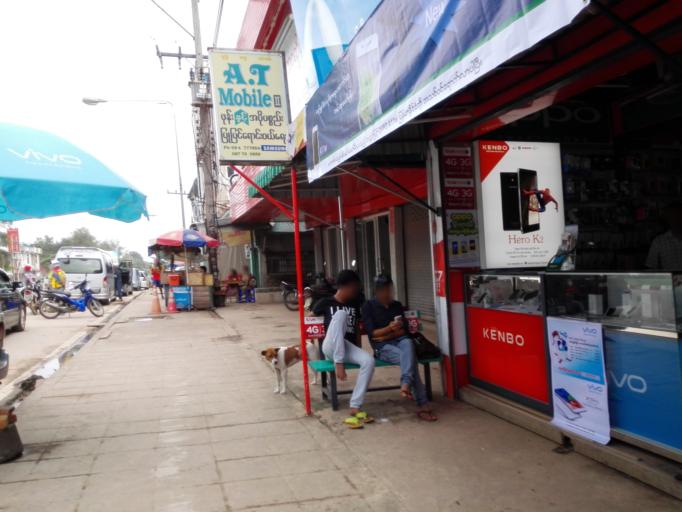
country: TH
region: Tak
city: Mae Sot
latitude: 16.6867
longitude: 98.4996
